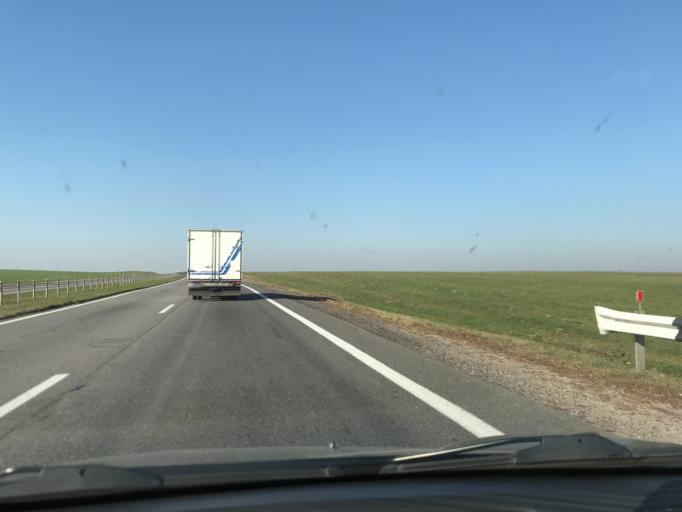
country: BY
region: Minsk
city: Dukora
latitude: 53.6771
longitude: 27.9287
